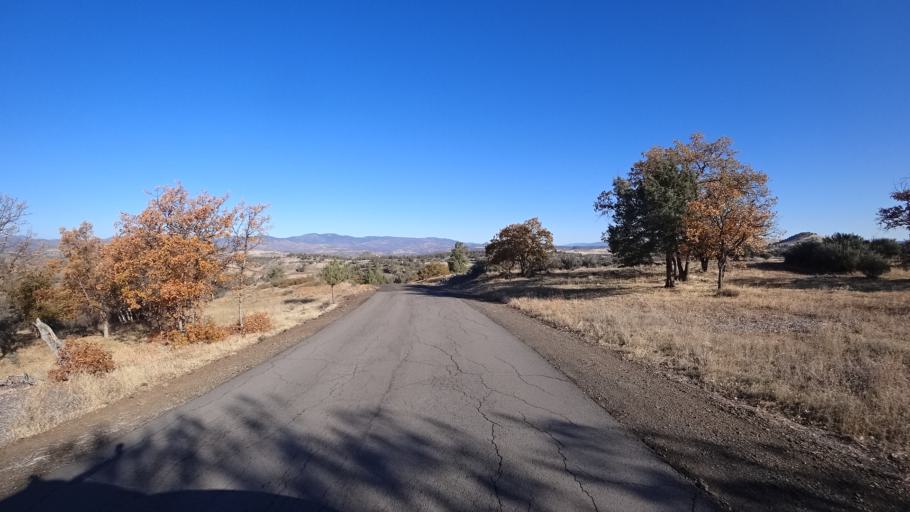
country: US
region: California
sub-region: Siskiyou County
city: Montague
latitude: 41.9079
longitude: -122.4361
